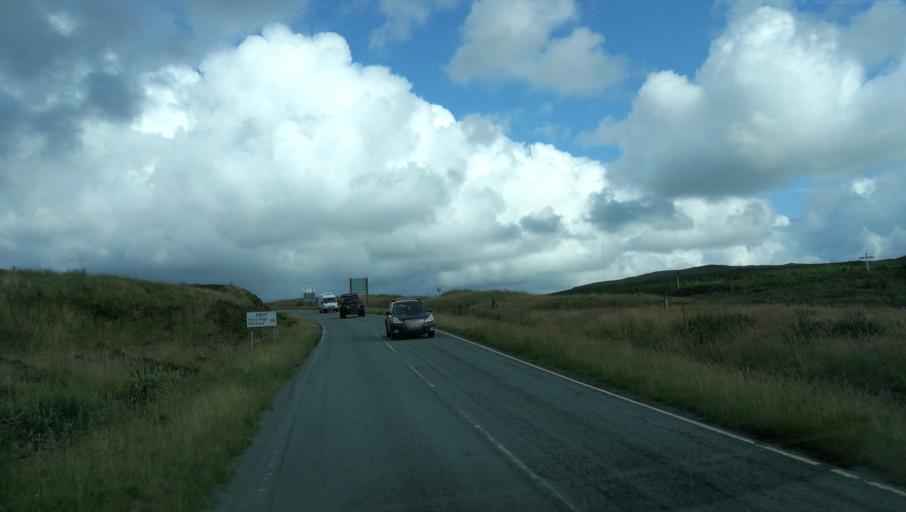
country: GB
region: Scotland
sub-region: Highland
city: Isle of Skye
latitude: 57.4693
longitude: -6.5361
